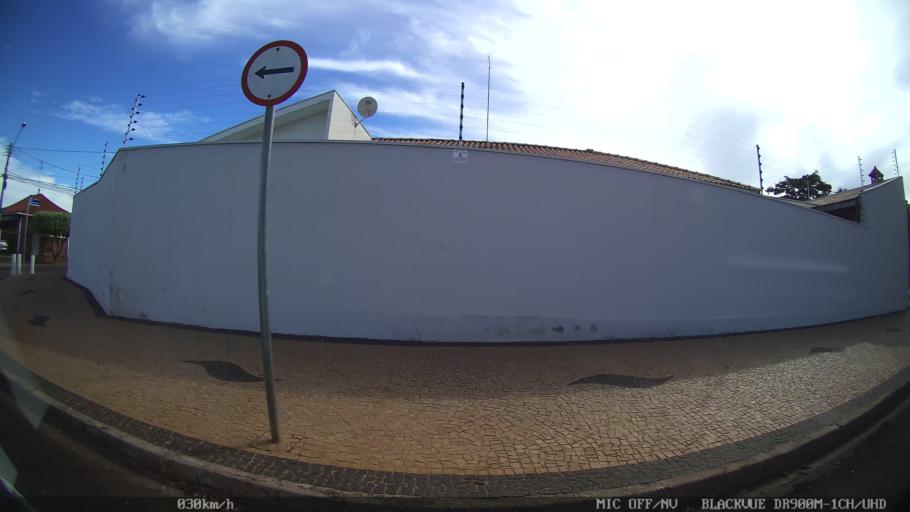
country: BR
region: Sao Paulo
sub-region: Catanduva
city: Catanduva
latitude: -21.1164
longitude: -48.9691
